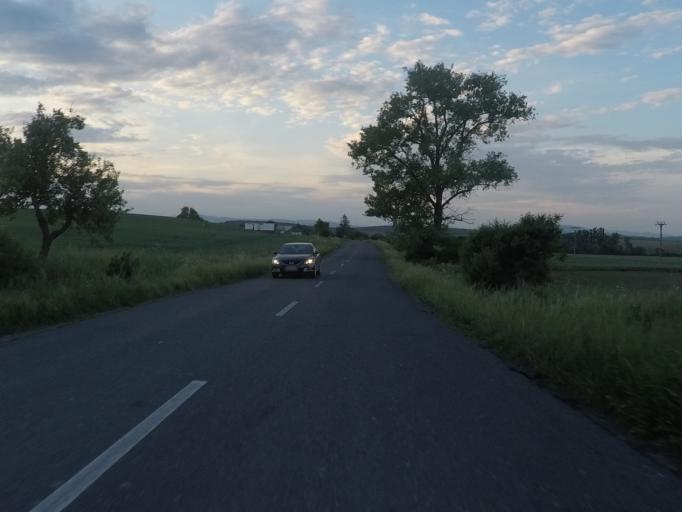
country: SK
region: Banskobystricky
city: Poltar
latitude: 48.3573
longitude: 19.8317
